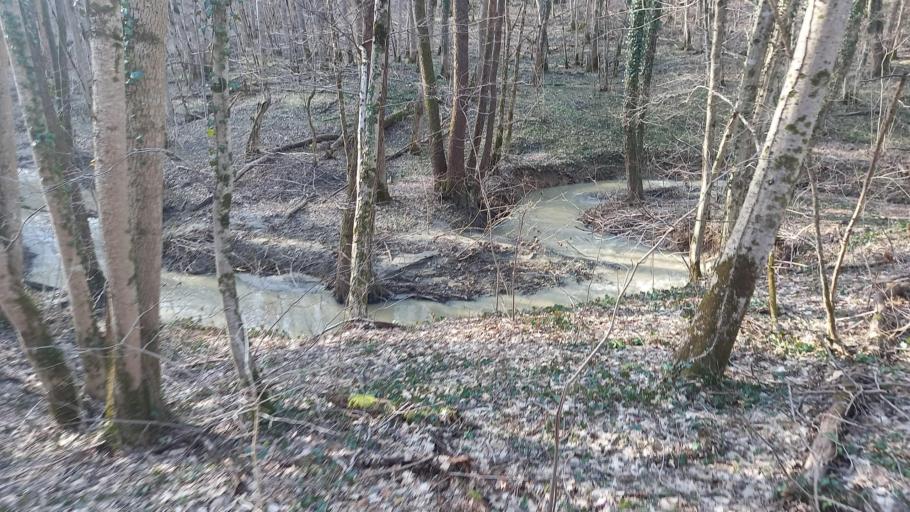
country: RU
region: Krasnodarskiy
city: Goryachiy Klyuch
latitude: 44.6903
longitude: 38.9737
